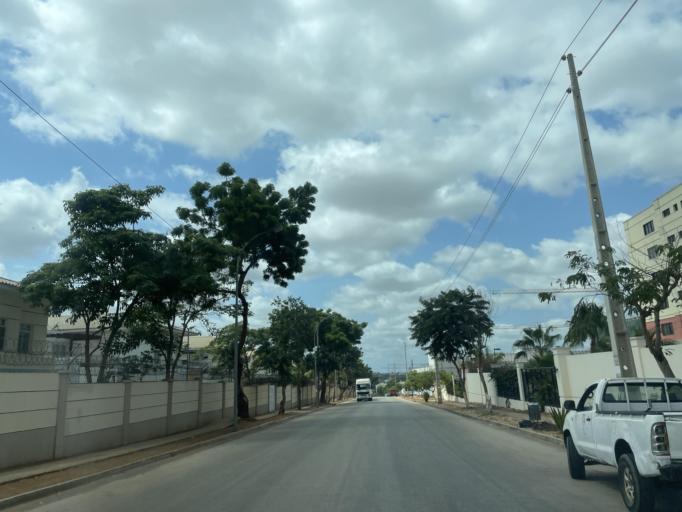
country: AO
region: Luanda
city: Luanda
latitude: -8.9280
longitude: 13.1841
